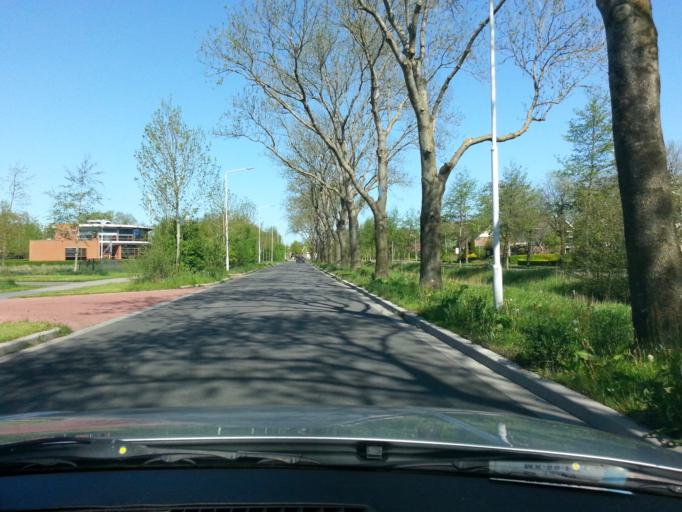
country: NL
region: Friesland
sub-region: Gemeente Achtkarspelen
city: Buitenpost
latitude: 53.2461
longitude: 6.1528
